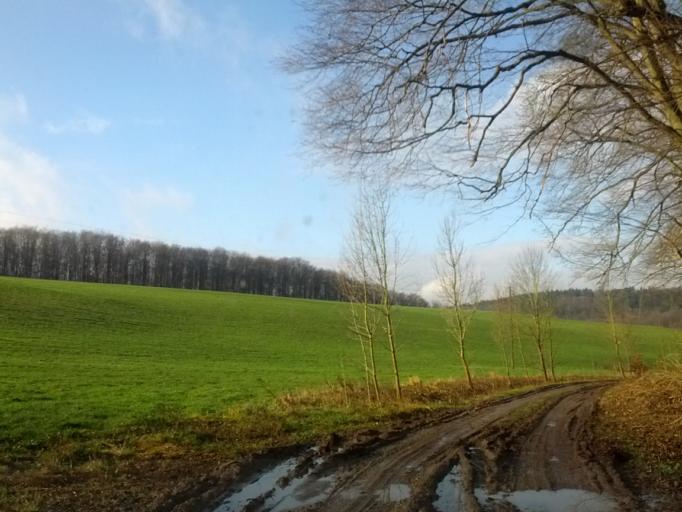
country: DE
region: Thuringia
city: Wolfsburg-Unkeroda
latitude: 50.9637
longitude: 10.2278
